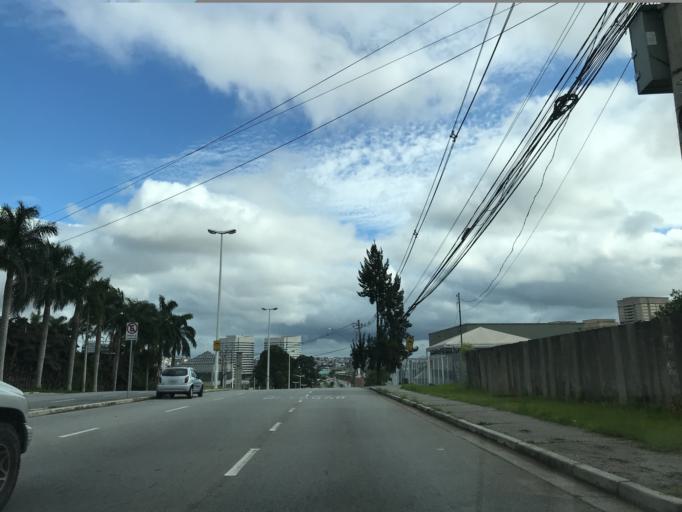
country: BR
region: Sao Paulo
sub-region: Carapicuiba
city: Carapicuiba
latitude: -23.4962
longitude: -46.8363
